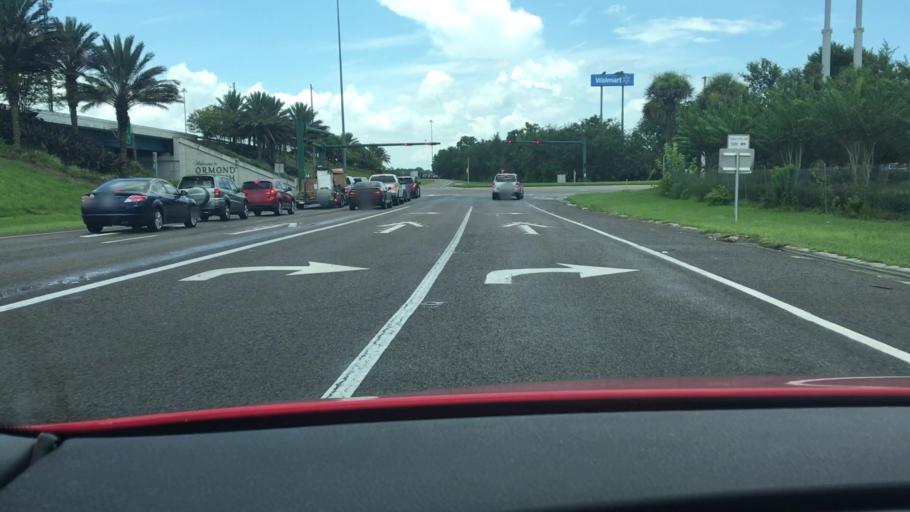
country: US
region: Florida
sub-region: Volusia County
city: Ormond Beach
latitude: 29.2563
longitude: -81.1151
